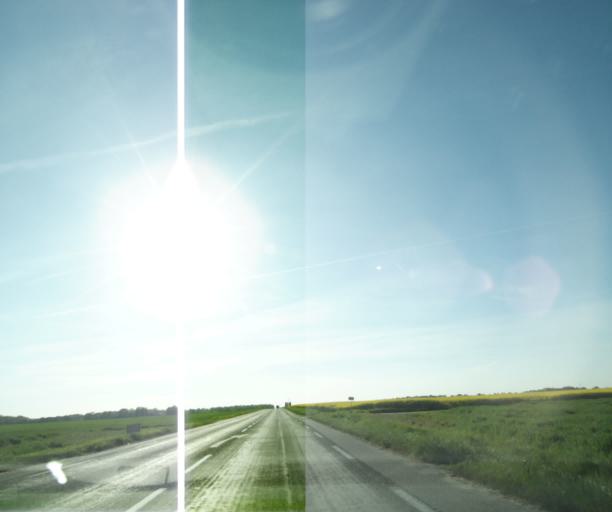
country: FR
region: Ile-de-France
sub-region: Departement de Seine-et-Marne
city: Nangis
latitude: 48.5564
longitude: 2.9897
